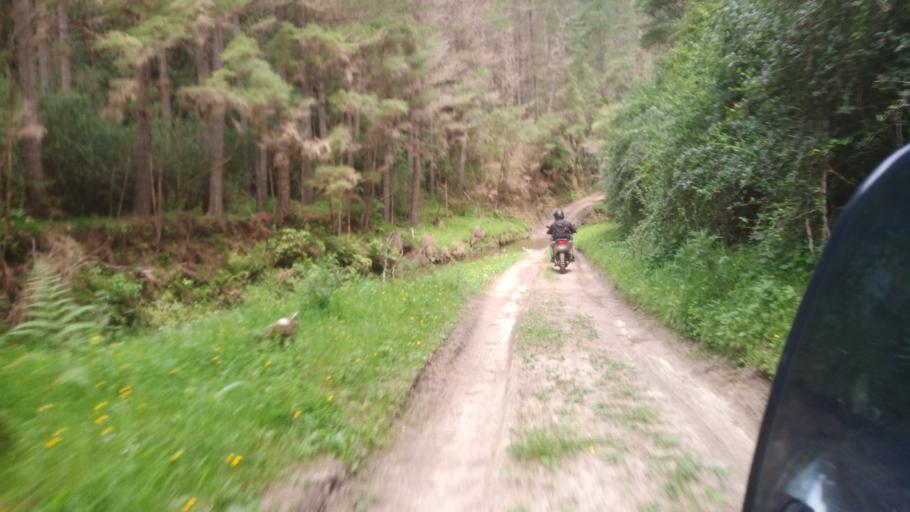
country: NZ
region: Gisborne
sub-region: Gisborne District
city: Gisborne
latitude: -38.4561
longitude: 177.9261
